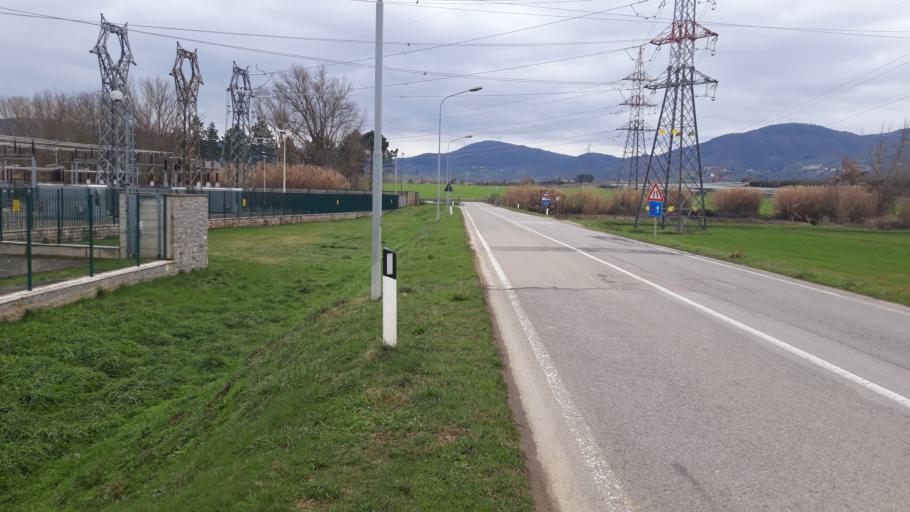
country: IT
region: Umbria
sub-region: Provincia di Perugia
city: Fontignano
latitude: 43.0042
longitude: 12.1797
